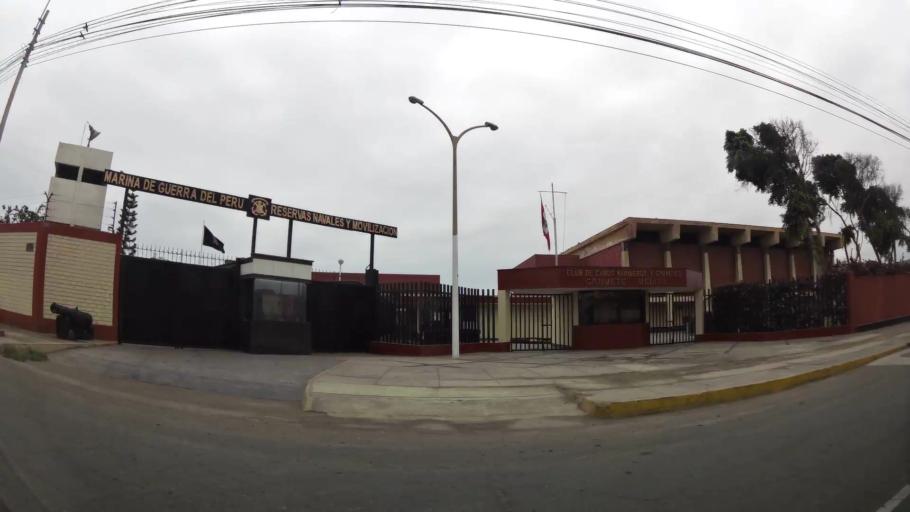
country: PE
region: Callao
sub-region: Callao
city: Callao
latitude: -12.0653
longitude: -77.1497
